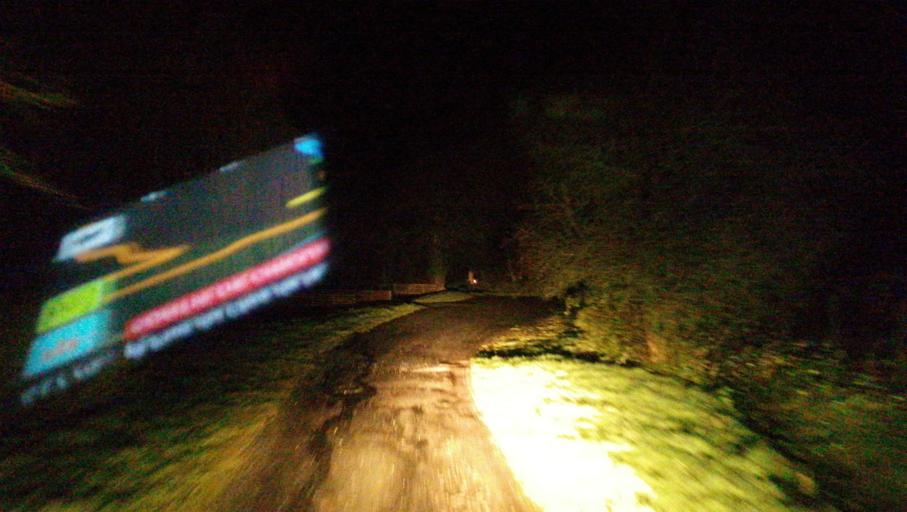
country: FR
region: Brittany
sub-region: Departement des Cotes-d'Armor
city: Plouagat
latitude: 48.4844
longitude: -2.9588
